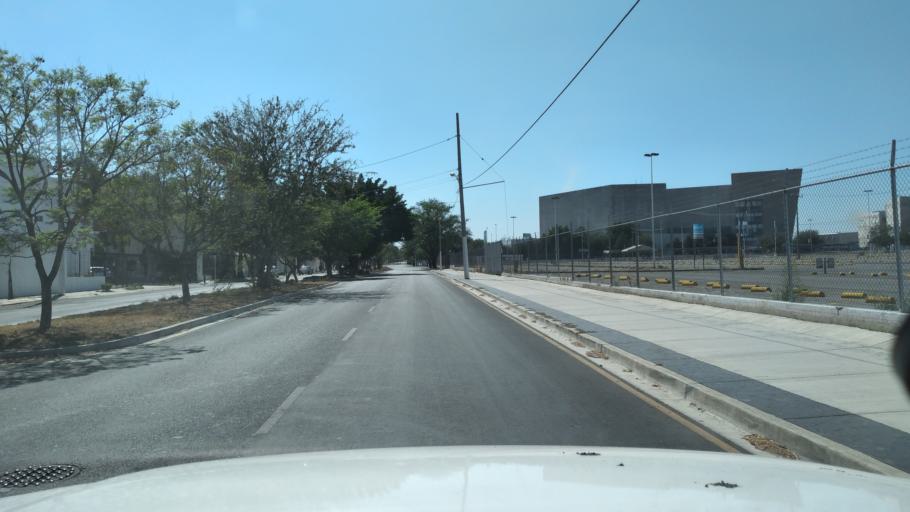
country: MX
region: Jalisco
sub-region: Zapopan
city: Zapopan
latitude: 20.7317
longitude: -103.3780
